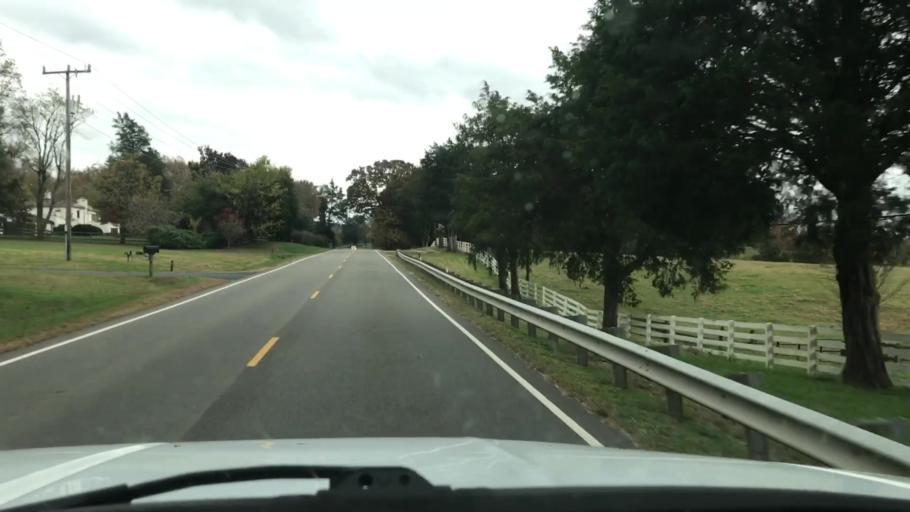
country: US
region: Virginia
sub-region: Goochland County
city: Goochland
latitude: 37.6419
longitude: -77.8157
